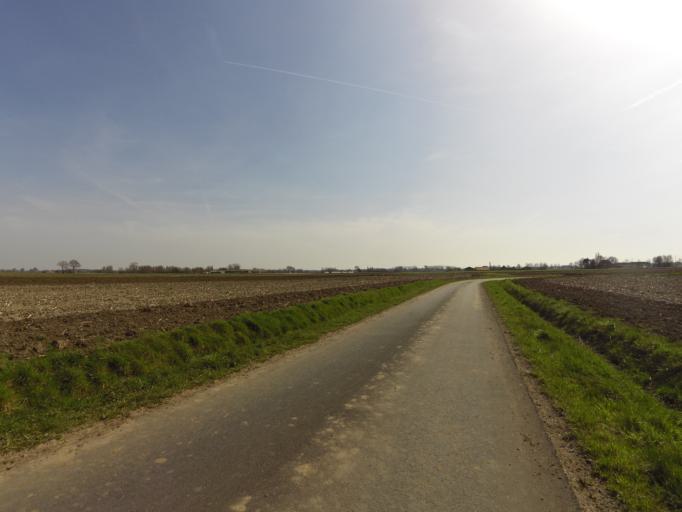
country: BE
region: Flanders
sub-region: Provincie West-Vlaanderen
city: Koekelare
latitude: 51.1095
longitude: 2.9469
